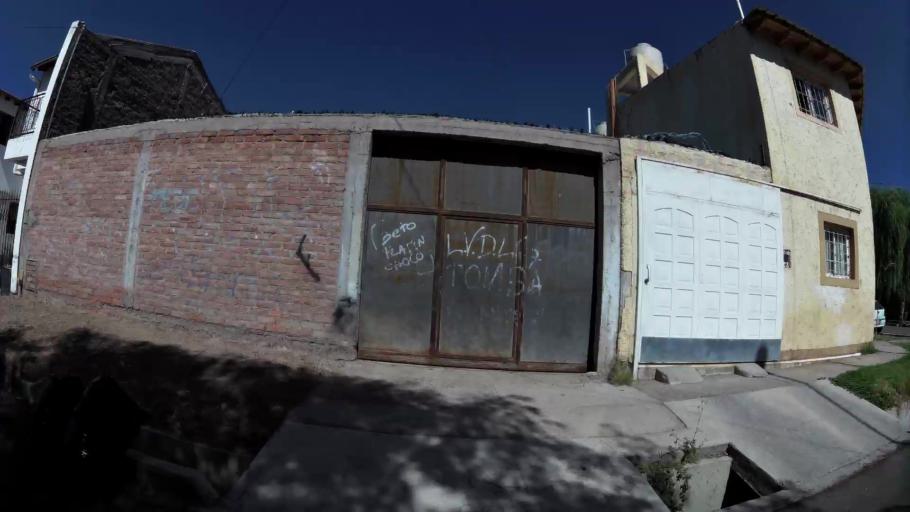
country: AR
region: Mendoza
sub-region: Departamento de Godoy Cruz
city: Godoy Cruz
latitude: -32.9189
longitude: -68.8795
